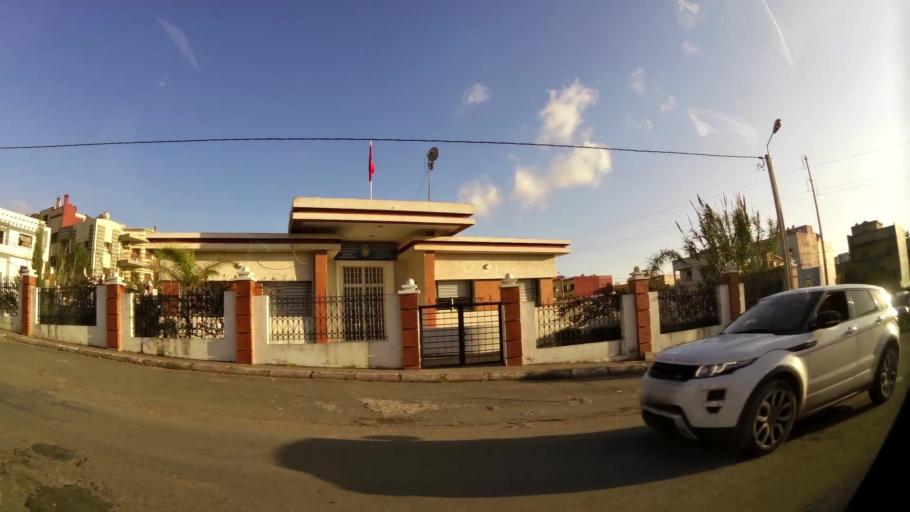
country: MA
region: Chaouia-Ouardigha
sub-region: Settat Province
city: Settat
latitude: 33.0090
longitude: -7.6089
